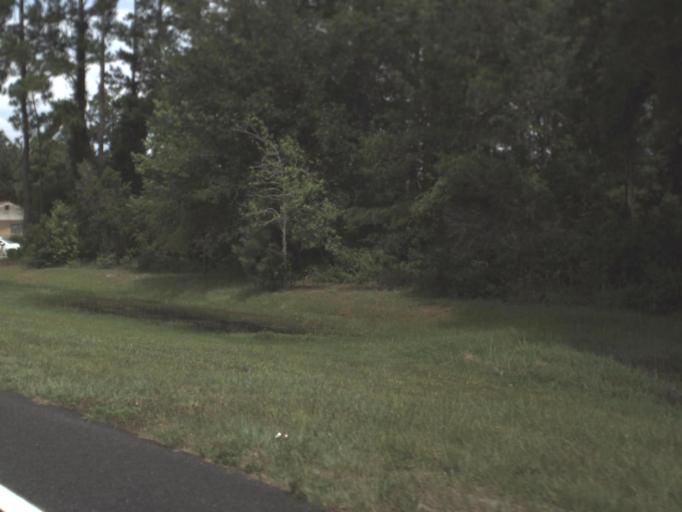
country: US
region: Florida
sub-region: Alachua County
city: Hawthorne
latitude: 29.6029
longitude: -82.2065
